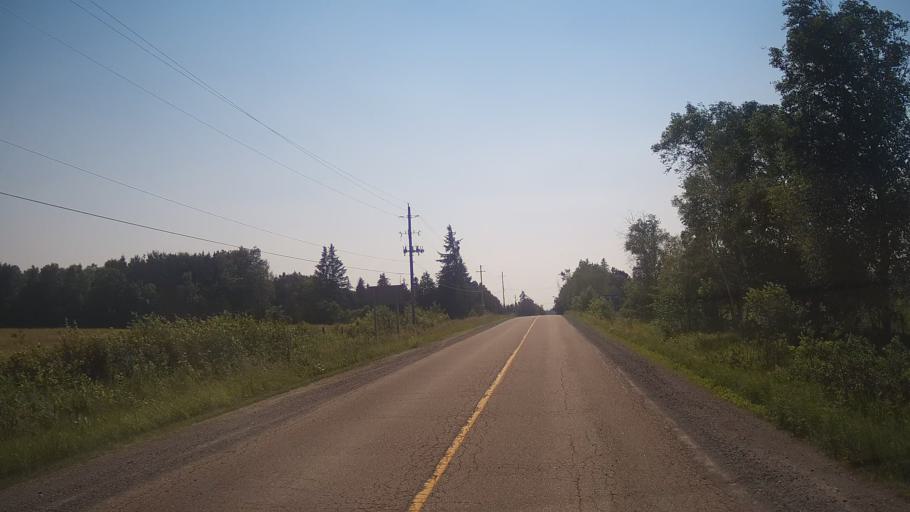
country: CA
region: Ontario
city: Pembroke
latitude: 45.5841
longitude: -77.2327
